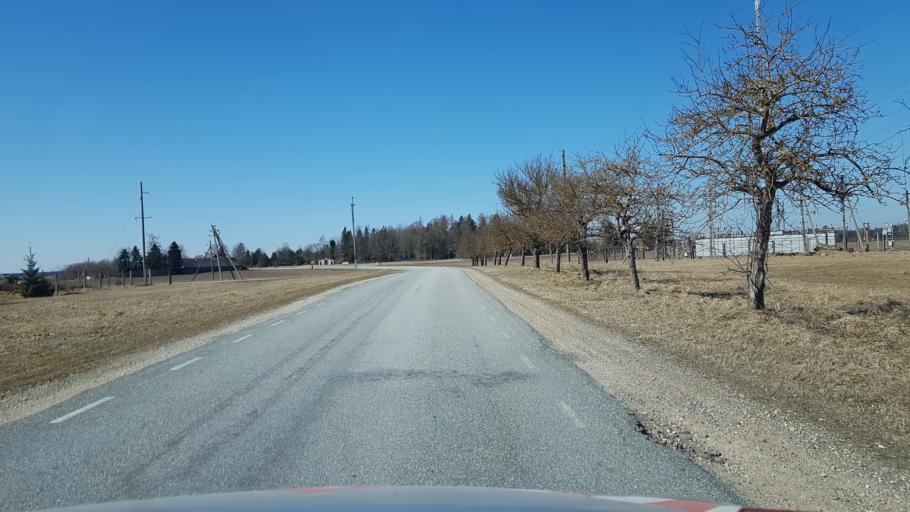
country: EE
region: Laeaene-Virumaa
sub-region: Rakke vald
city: Rakke
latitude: 59.0483
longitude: 26.3843
